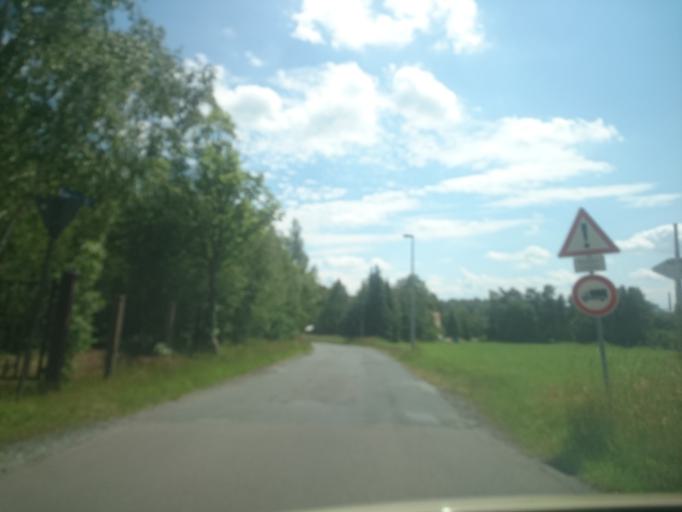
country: DE
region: Saxony
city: Brand-Erbisdorf
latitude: 50.8791
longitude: 13.3382
